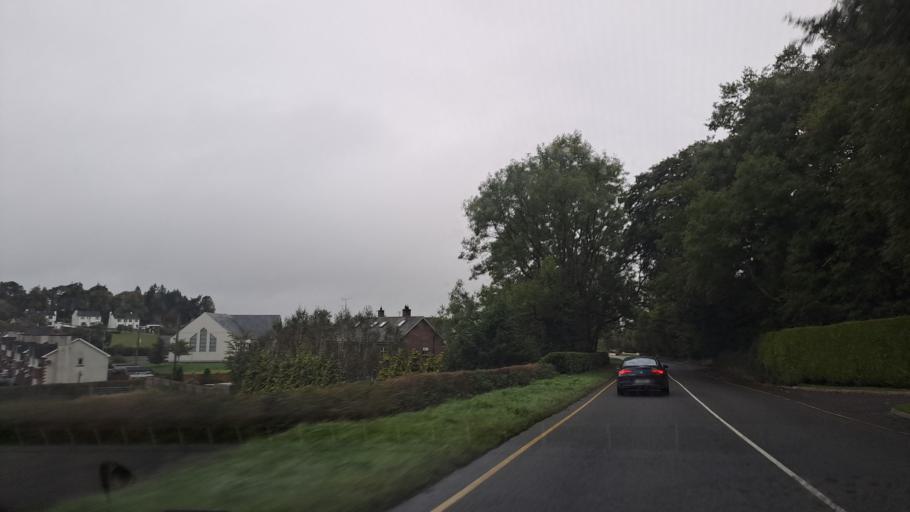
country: IE
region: Ulster
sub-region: County Monaghan
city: Monaghan
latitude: 54.2329
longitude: -6.9625
